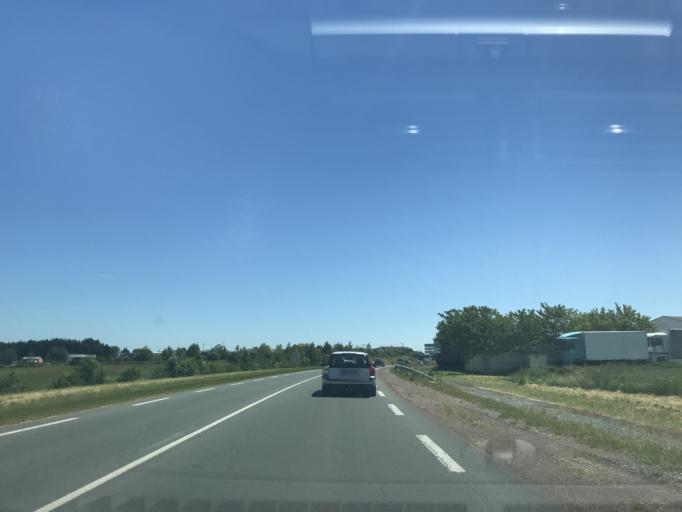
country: FR
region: Poitou-Charentes
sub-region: Departement de la Charente-Maritime
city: Saint-Georges-de-Didonne
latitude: 45.6094
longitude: -0.9771
